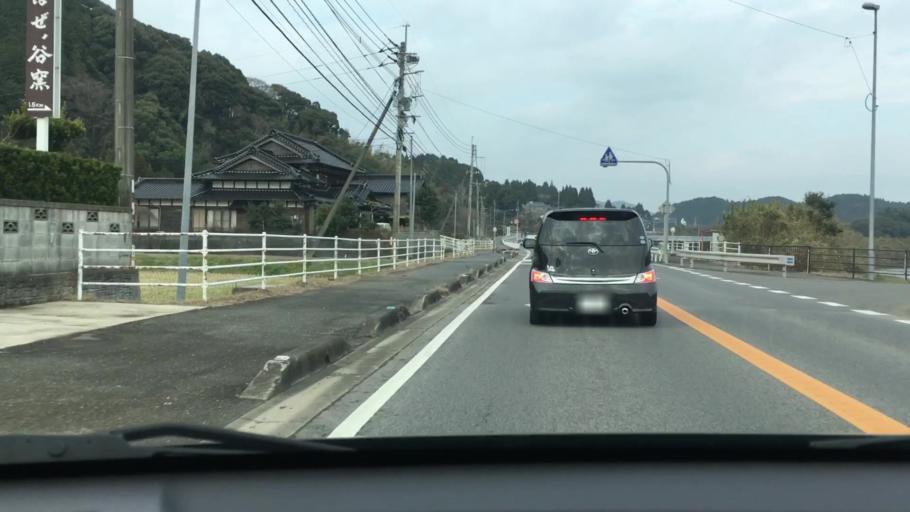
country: JP
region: Saga Prefecture
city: Imaricho-ko
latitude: 33.3272
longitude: 129.9300
